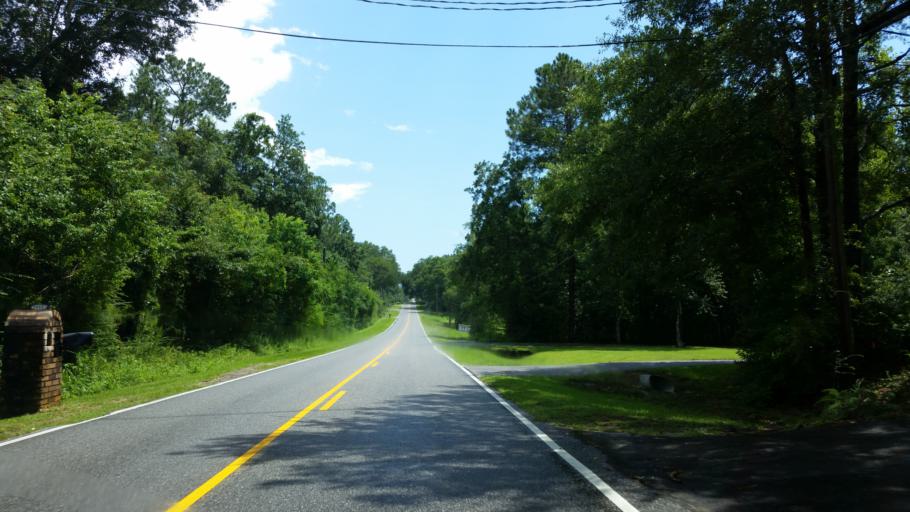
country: US
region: Florida
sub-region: Escambia County
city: Gonzalez
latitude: 30.5600
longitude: -87.2997
